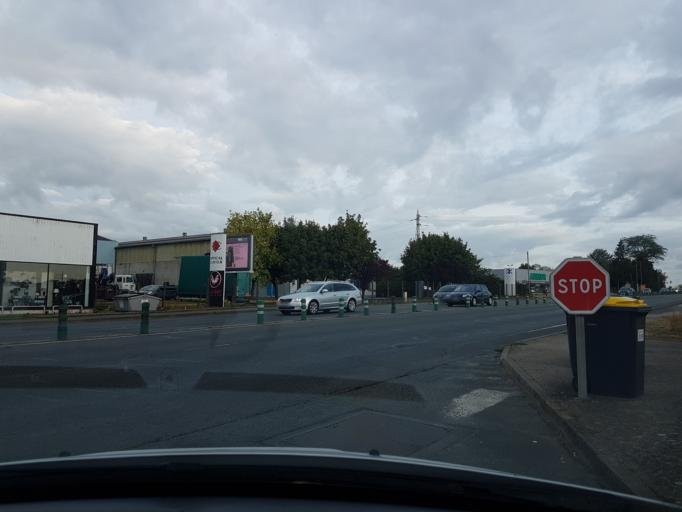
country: FR
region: Centre
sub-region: Departement d'Indre-et-Loire
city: Chambray-les-Tours
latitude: 47.3414
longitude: 0.7035
